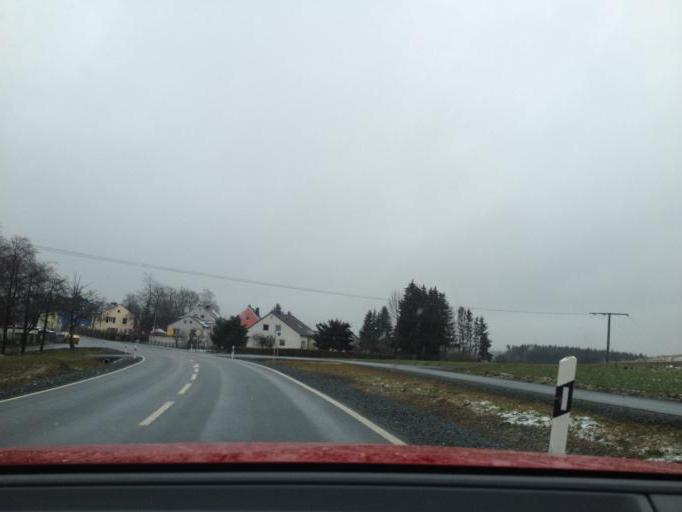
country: DE
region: Bavaria
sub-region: Upper Franconia
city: Dohlau
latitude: 50.3178
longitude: 11.9564
